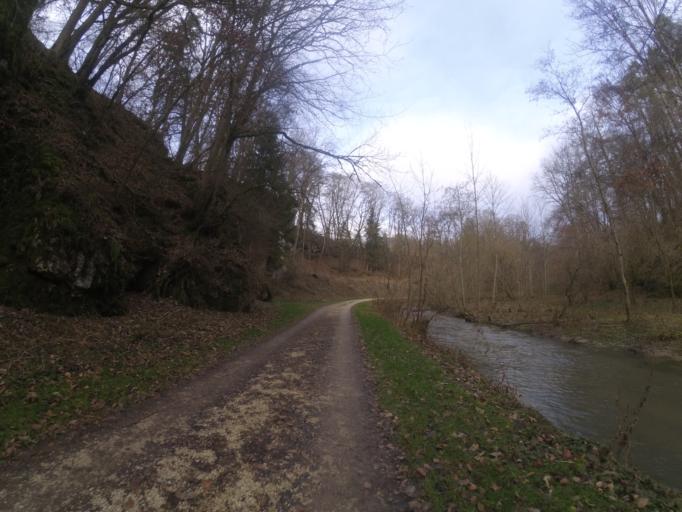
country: DE
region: Baden-Wuerttemberg
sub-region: Tuebingen Region
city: Lauterach
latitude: 48.2478
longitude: 9.5800
